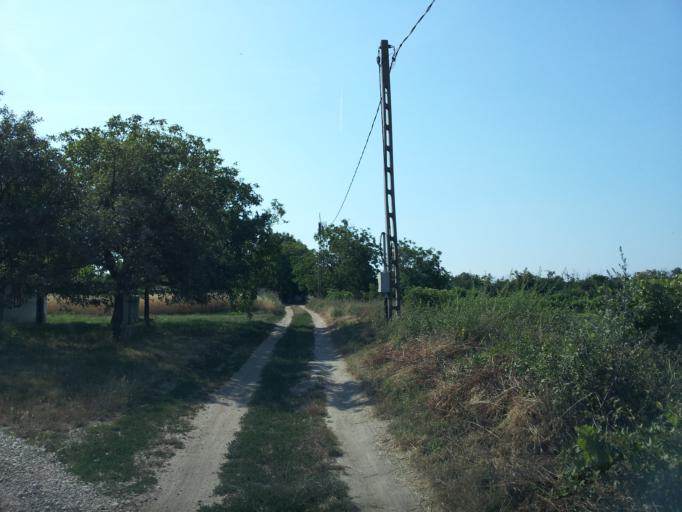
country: HU
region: Fejer
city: Lovasbereny
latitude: 47.3812
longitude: 18.5847
